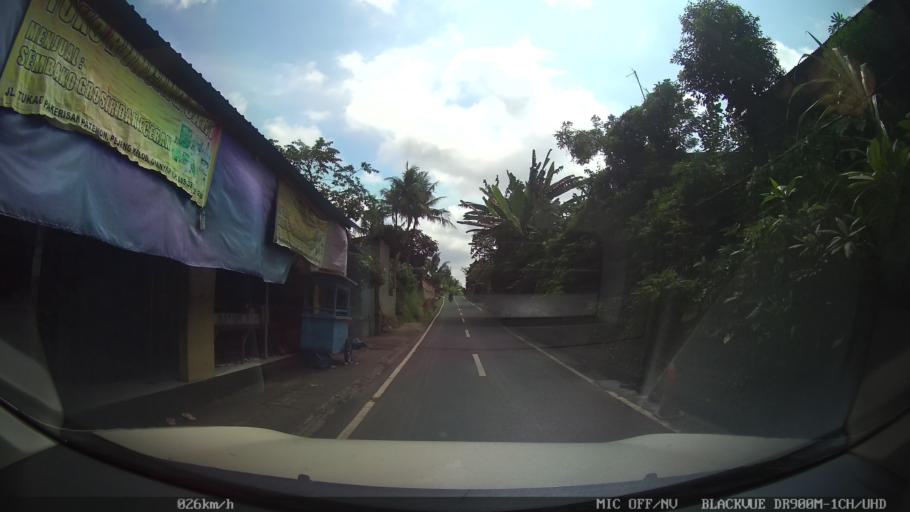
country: ID
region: Bali
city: Banjar Pesalakan
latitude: -8.5194
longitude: 115.3056
